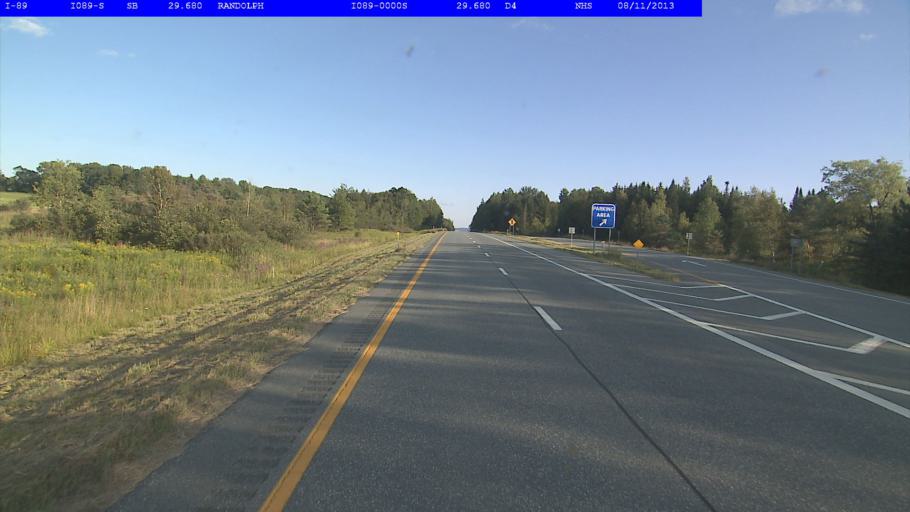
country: US
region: Vermont
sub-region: Orange County
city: Randolph
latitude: 43.9278
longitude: -72.6181
